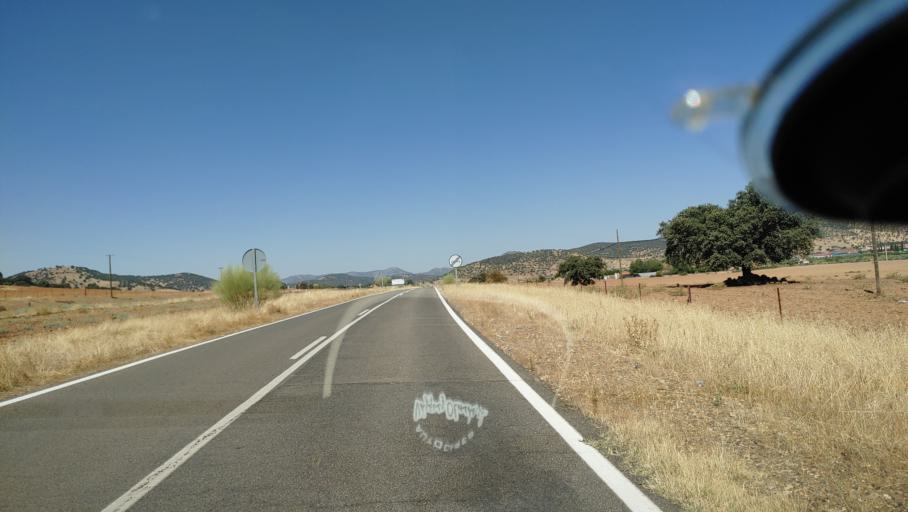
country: ES
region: Castille-La Mancha
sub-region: Provincia de Ciudad Real
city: Guadalmez
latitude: 38.7113
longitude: -4.9672
